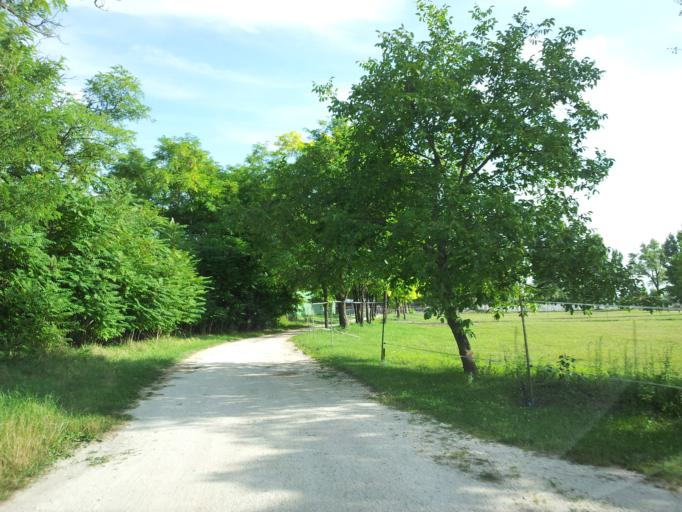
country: HU
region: Pest
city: Kiskunlachaza
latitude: 47.1960
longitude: 19.0017
